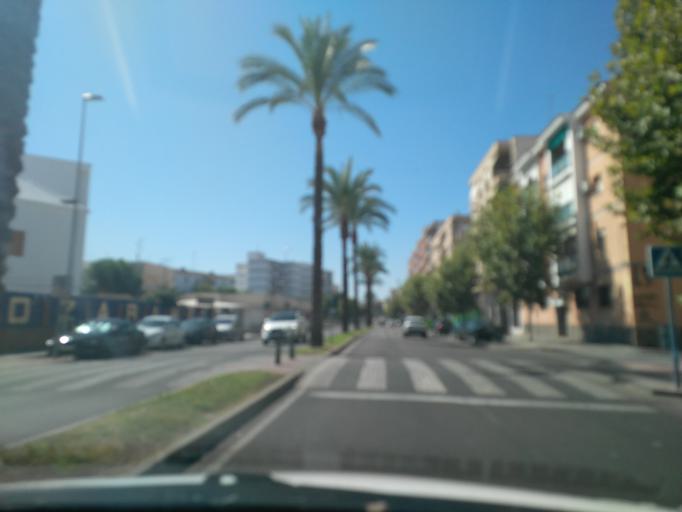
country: ES
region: Extremadura
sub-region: Provincia de Badajoz
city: Merida
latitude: 38.9229
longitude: -6.3296
